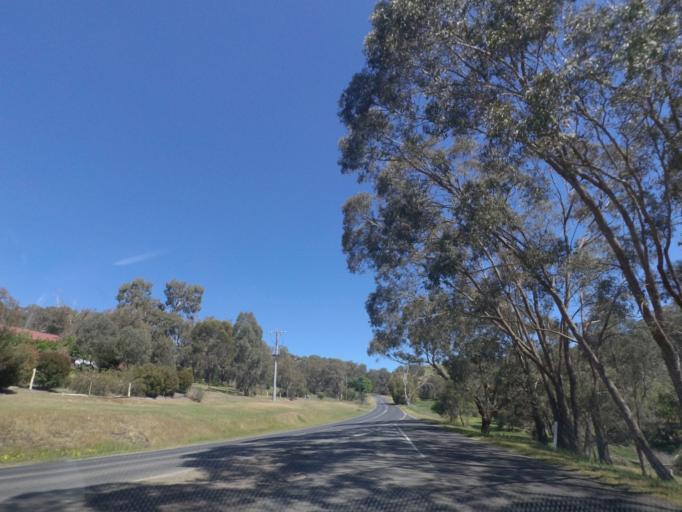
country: AU
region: Victoria
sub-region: Whittlesea
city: Whittlesea
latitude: -37.2885
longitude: 144.9788
